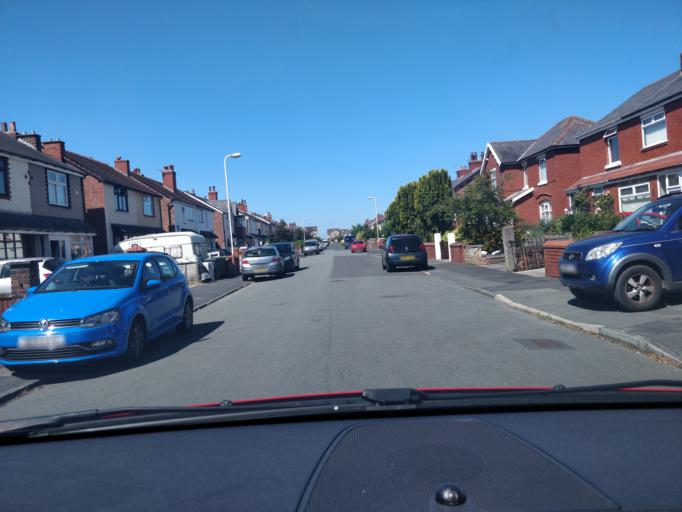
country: GB
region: England
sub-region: Lancashire
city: Banks
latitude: 53.6728
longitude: -2.9449
